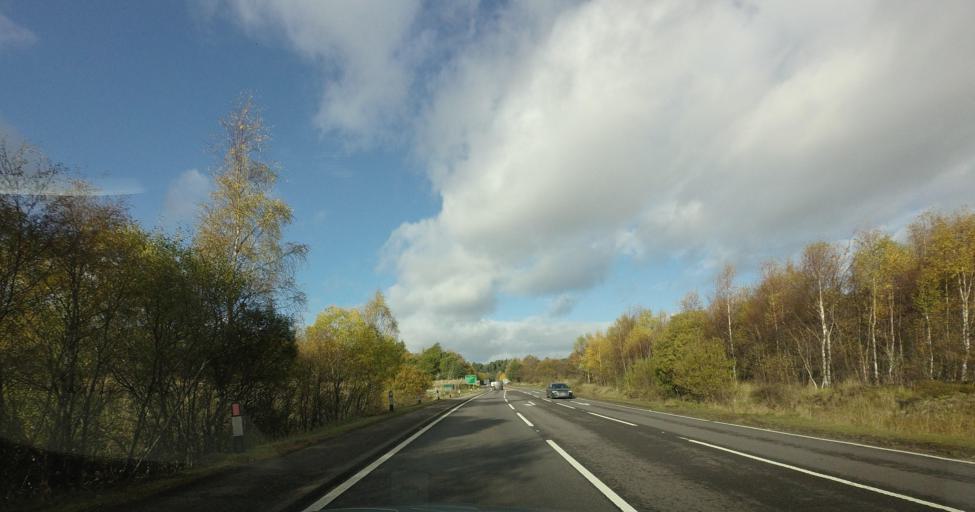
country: GB
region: Scotland
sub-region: Highland
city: Grantown on Spey
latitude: 57.3172
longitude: -3.6025
